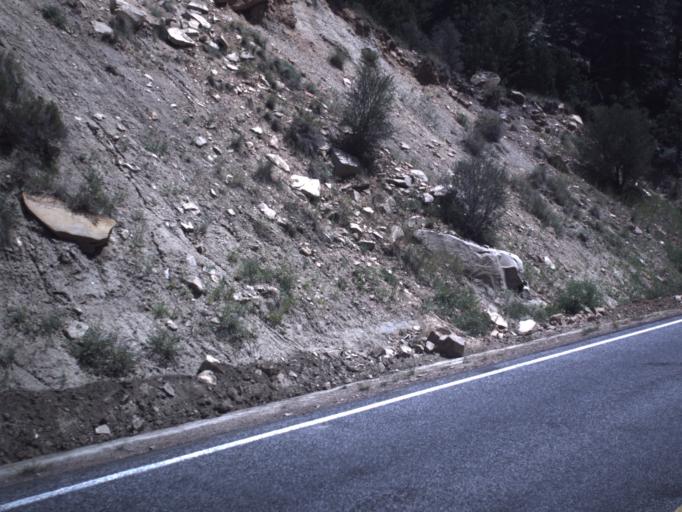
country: US
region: Utah
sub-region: Emery County
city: Huntington
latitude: 39.4508
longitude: -111.1401
